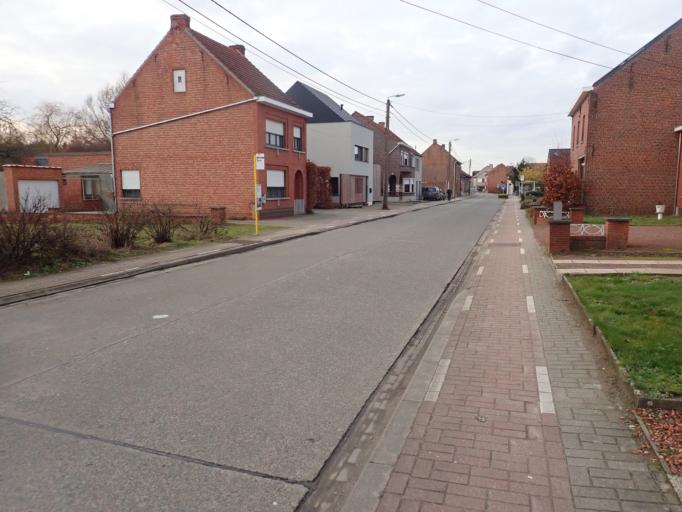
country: BE
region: Flanders
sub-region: Provincie Vlaams-Brabant
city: Holsbeek
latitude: 50.9518
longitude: 4.7523
